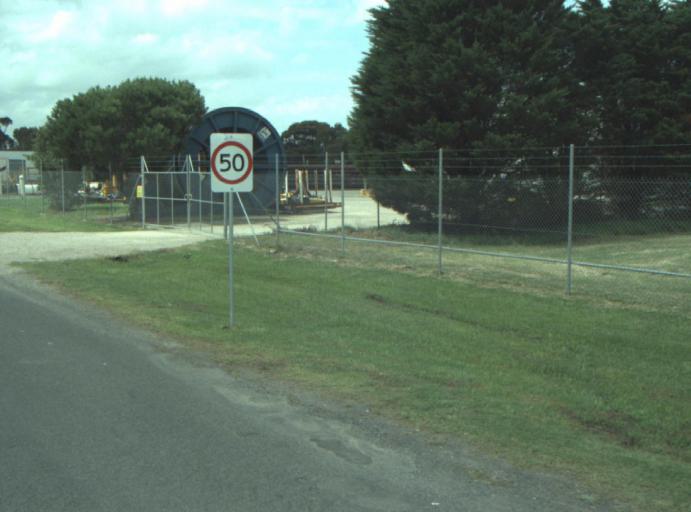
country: AU
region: Victoria
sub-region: Greater Geelong
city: East Geelong
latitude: -38.1744
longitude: 144.4070
